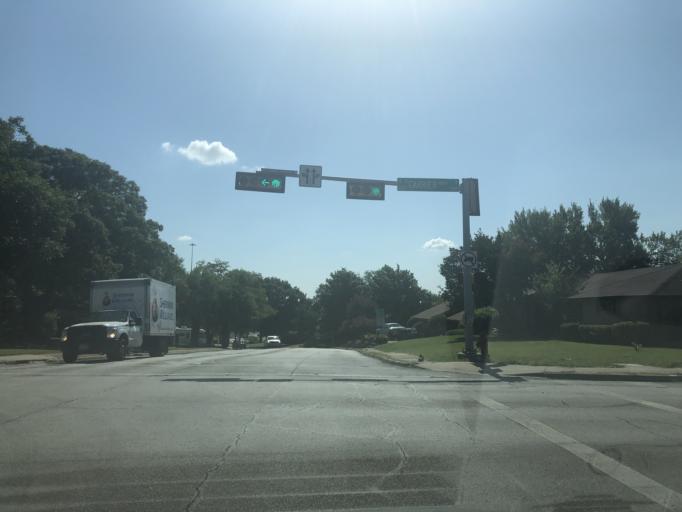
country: US
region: Texas
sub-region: Dallas County
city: Grand Prairie
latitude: 32.7584
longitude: -97.0200
